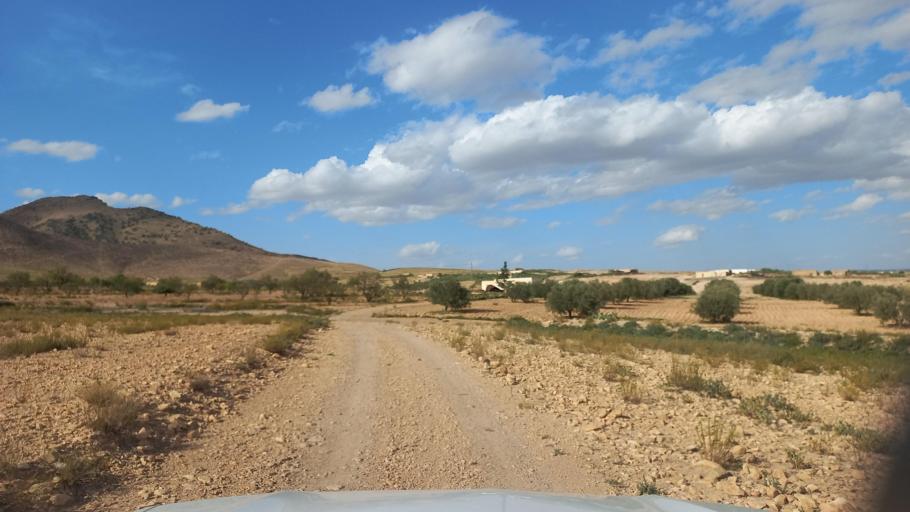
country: TN
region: Al Qasrayn
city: Sbiba
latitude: 35.4510
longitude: 9.0763
